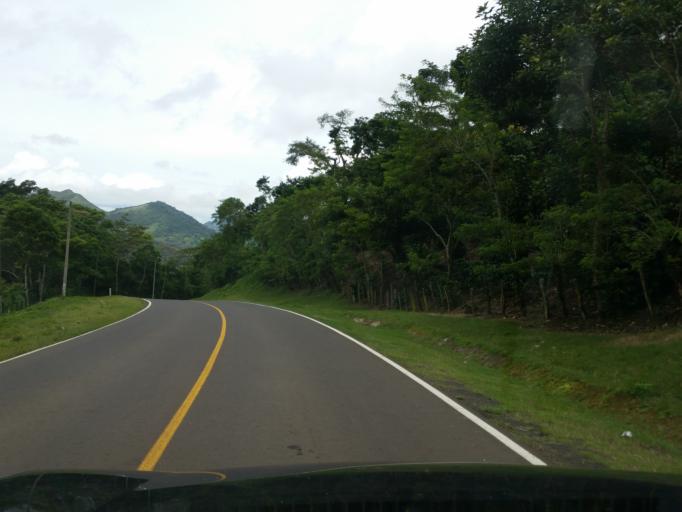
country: NI
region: Matagalpa
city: San Ramon
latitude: 12.9599
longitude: -85.8592
